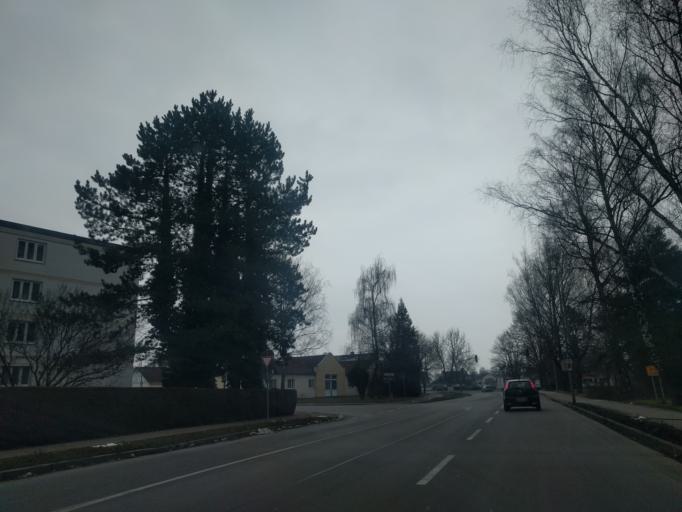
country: DE
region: Bavaria
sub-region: Swabia
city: Rain
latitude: 48.6936
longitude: 10.9091
